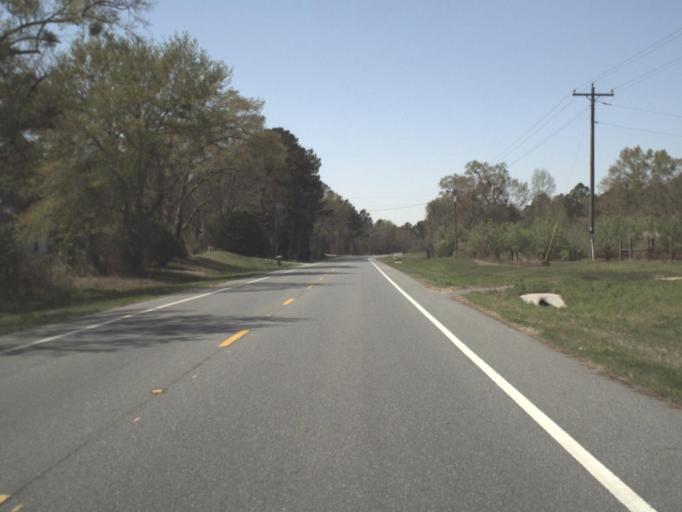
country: US
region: Florida
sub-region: Jackson County
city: Graceville
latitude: 30.9629
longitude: -85.6521
